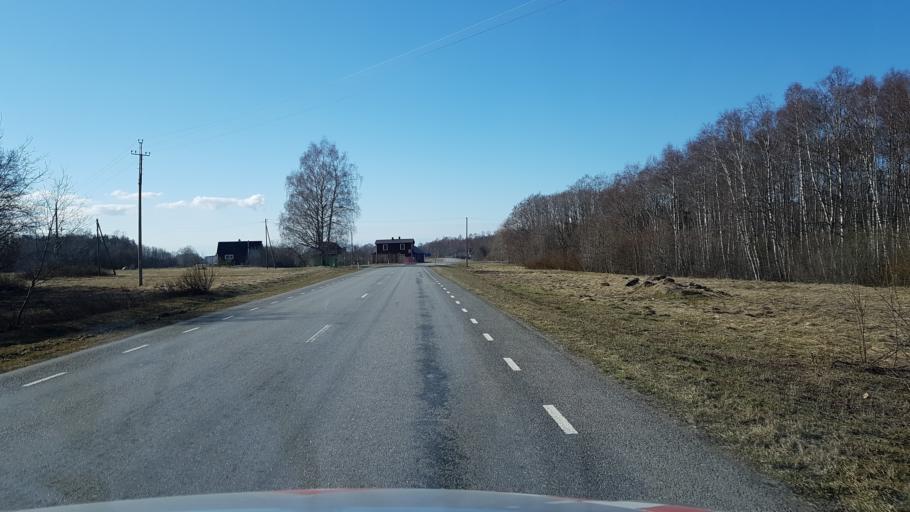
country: EE
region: Laeaene-Virumaa
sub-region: Haljala vald
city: Haljala
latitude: 59.4550
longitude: 26.2329
